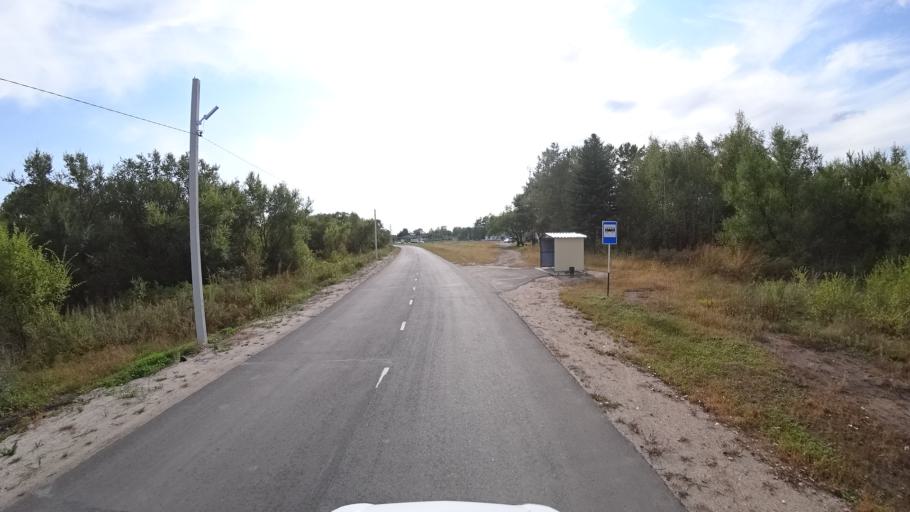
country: RU
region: Amur
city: Arkhara
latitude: 49.3642
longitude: 130.1242
